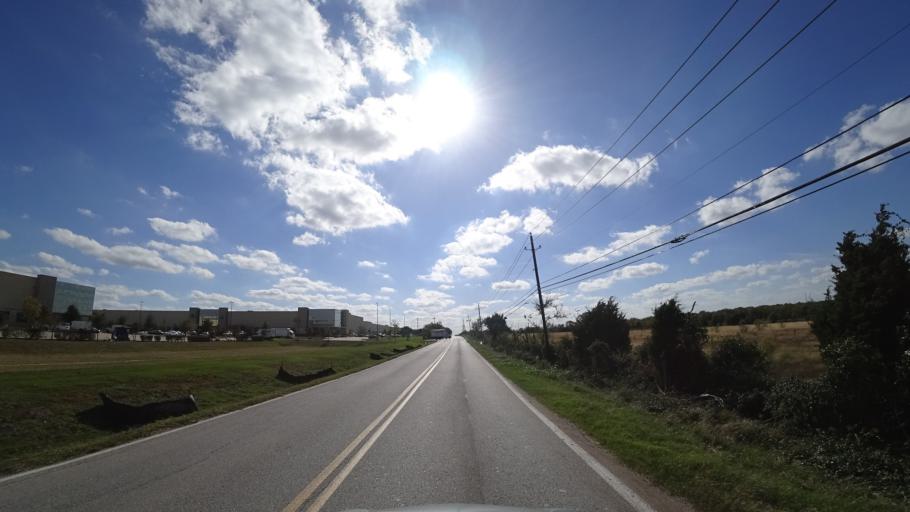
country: US
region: Texas
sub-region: Travis County
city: Wells Branch
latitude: 30.4633
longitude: -97.6740
